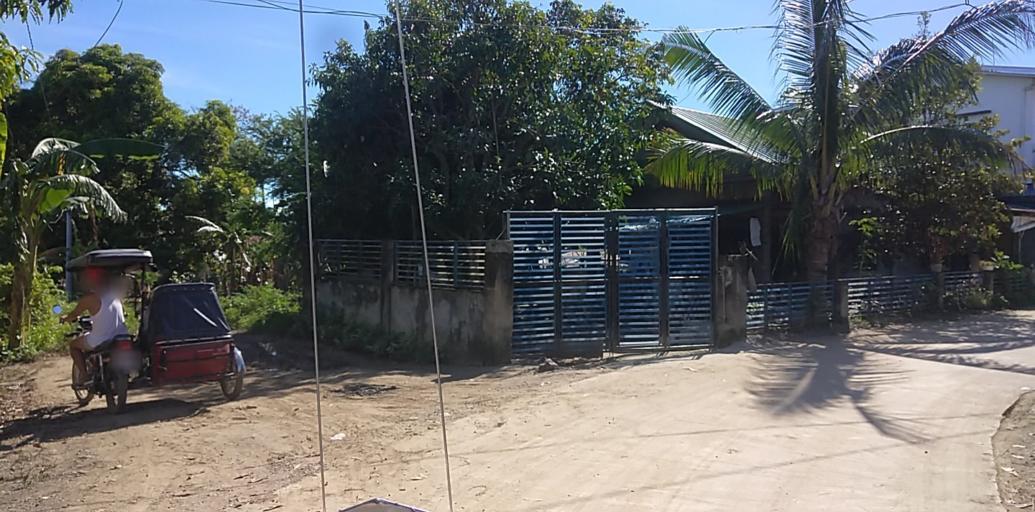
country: PH
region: Central Luzon
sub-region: Province of Pampanga
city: San Nicolas
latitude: 15.0645
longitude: 120.8106
